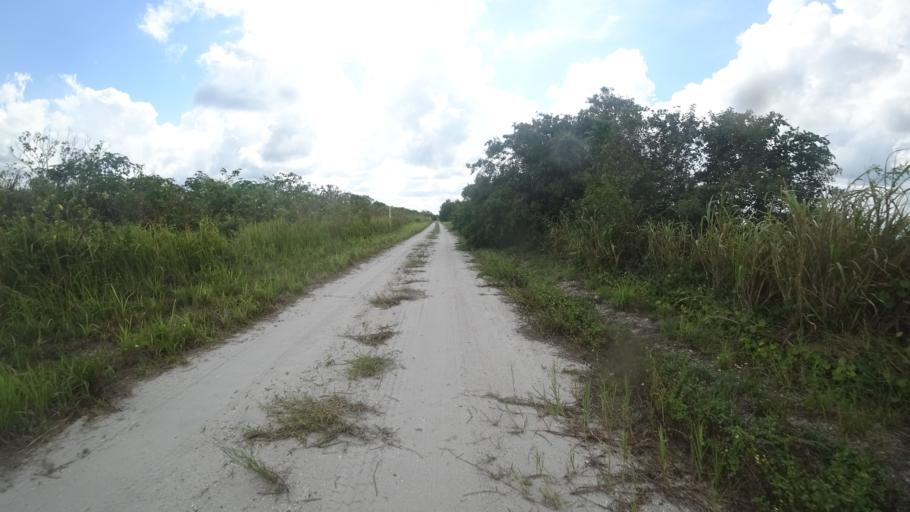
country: US
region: Florida
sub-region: Hillsborough County
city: Wimauma
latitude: 27.5804
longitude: -82.2674
